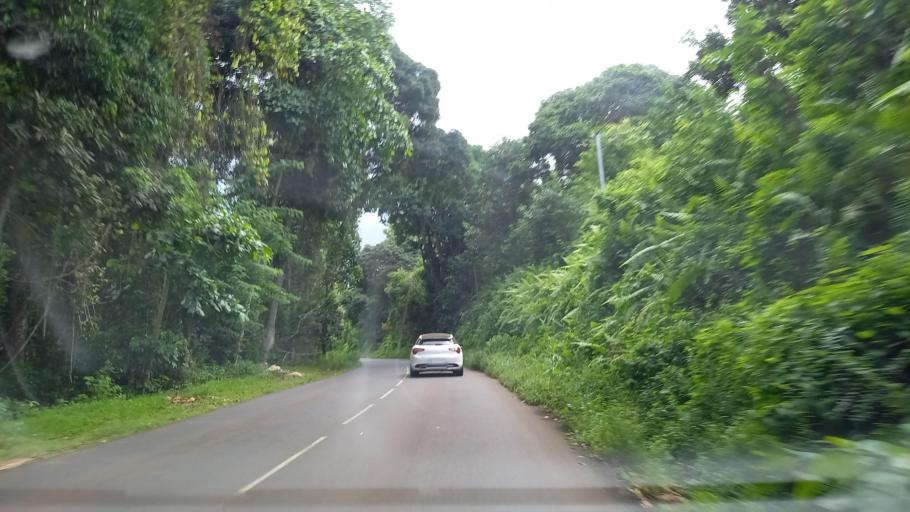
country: YT
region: Dembeni
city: Dembeni
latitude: -12.7876
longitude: 45.1676
